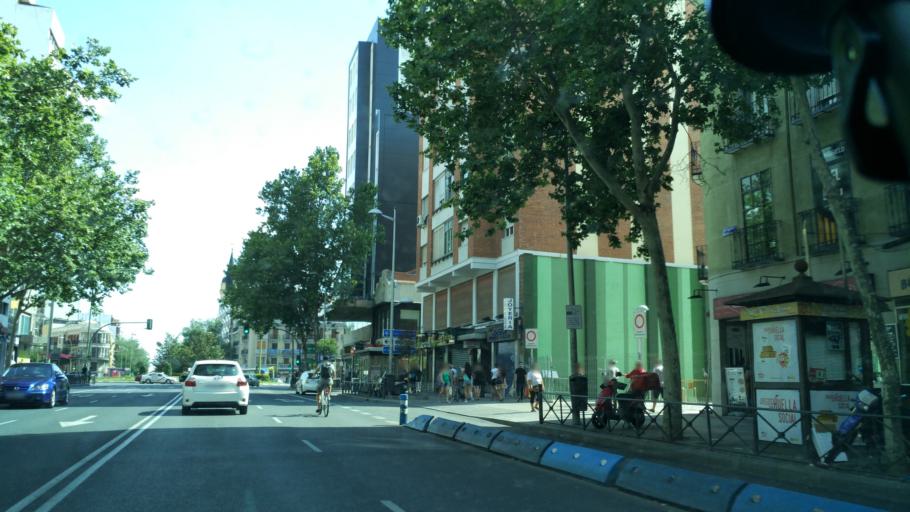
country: ES
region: Madrid
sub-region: Provincia de Madrid
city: Chamberi
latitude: 40.4482
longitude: -3.7038
